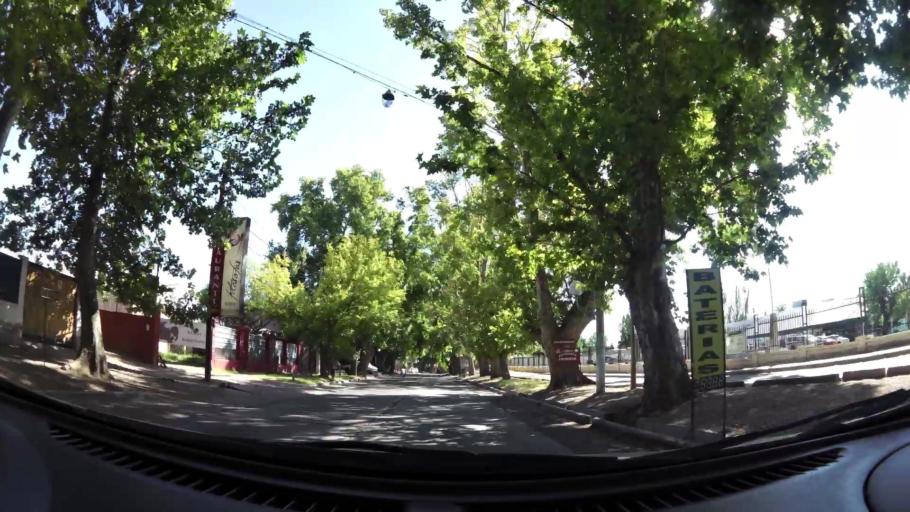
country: AR
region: Mendoza
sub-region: Departamento de Godoy Cruz
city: Godoy Cruz
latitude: -32.9799
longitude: -68.8590
